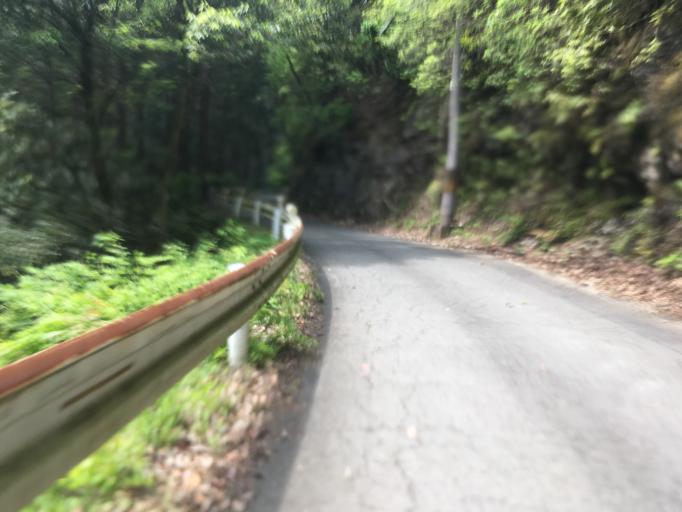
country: JP
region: Kyoto
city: Kameoka
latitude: 35.0298
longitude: 135.6356
